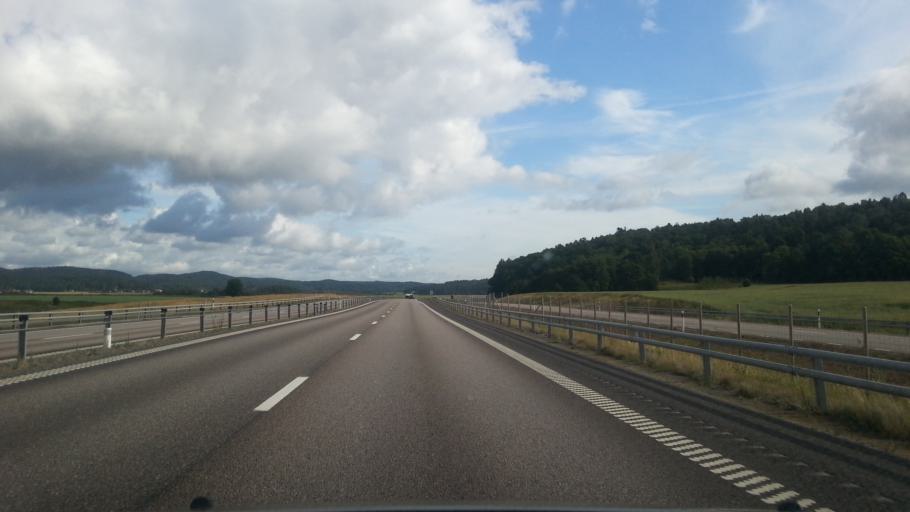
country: SE
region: Vaestra Goetaland
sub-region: Lilla Edets Kommun
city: Lilla Edet
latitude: 58.1894
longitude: 12.1450
